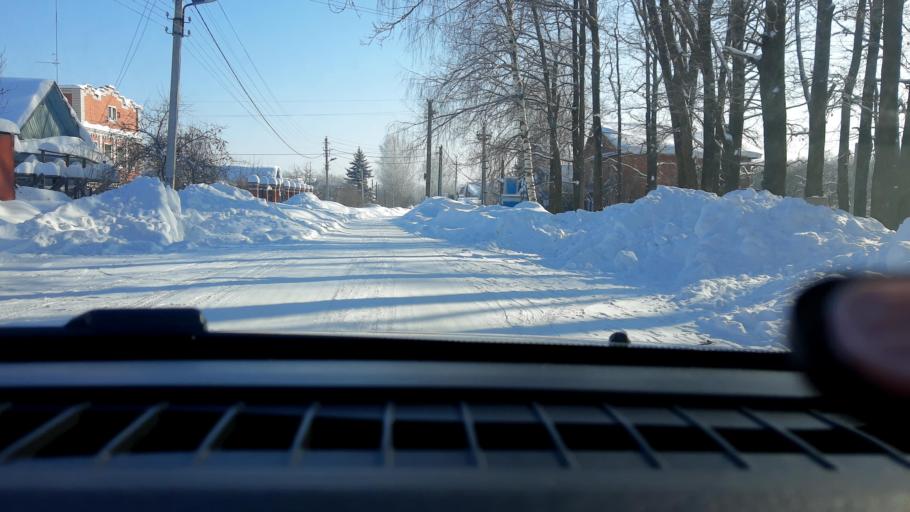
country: RU
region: Nizjnij Novgorod
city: Afonino
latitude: 56.1992
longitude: 44.0330
